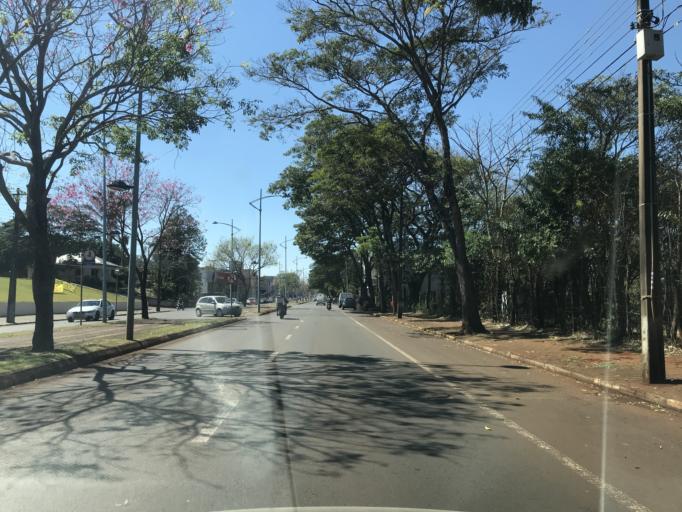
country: BR
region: Parana
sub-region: Toledo
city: Toledo
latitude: -24.7263
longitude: -53.7328
